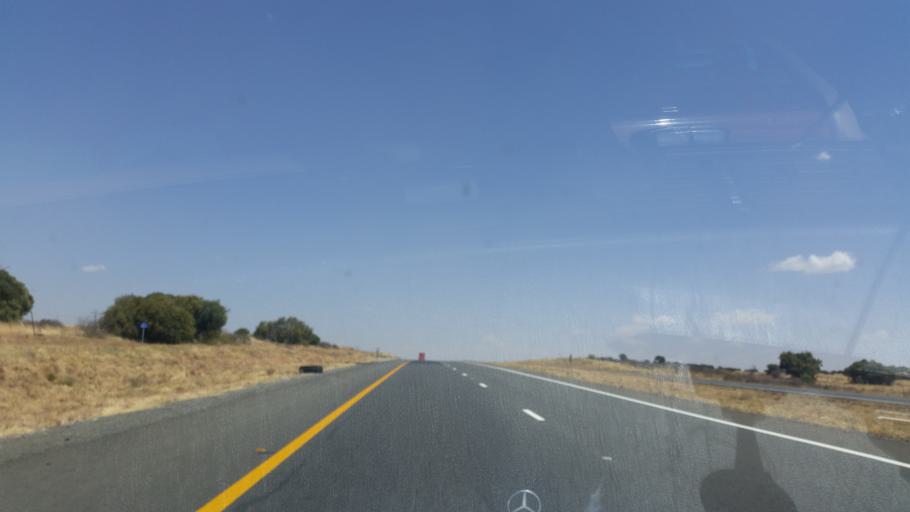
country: ZA
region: Orange Free State
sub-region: Lejweleputswa District Municipality
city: Brandfort
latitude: -28.9151
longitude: 26.4496
